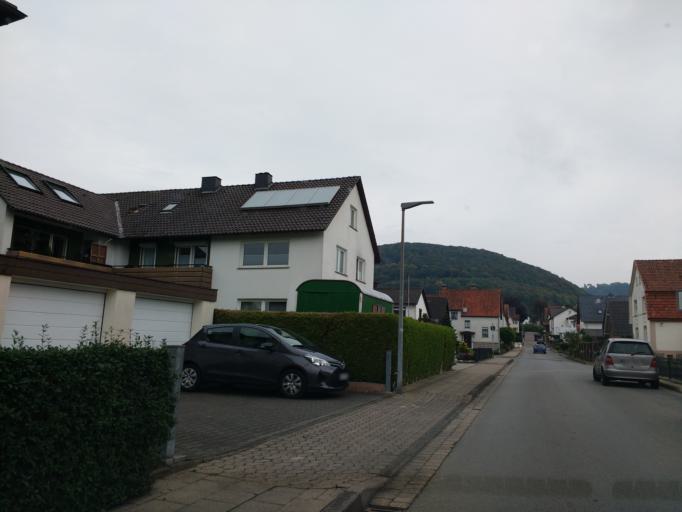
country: DE
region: North Rhine-Westphalia
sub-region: Regierungsbezirk Detmold
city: Lugde
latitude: 51.9628
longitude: 9.2488
